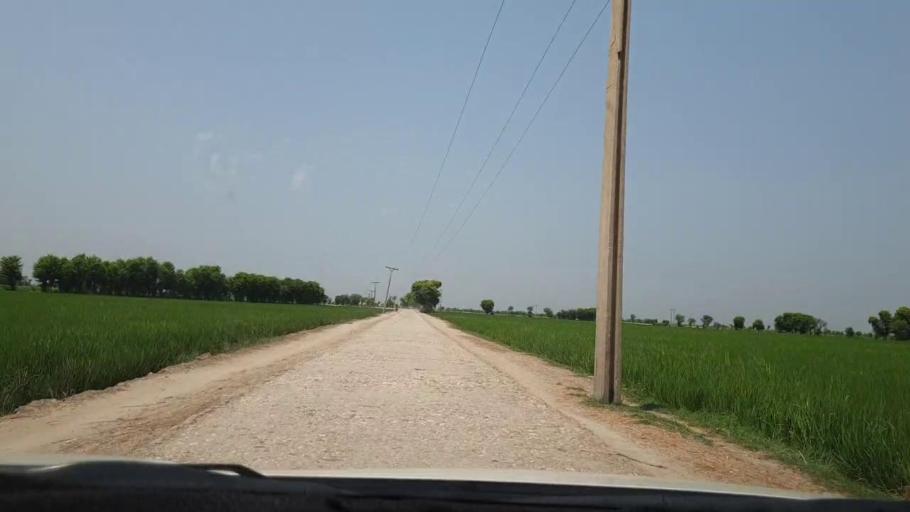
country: PK
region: Sindh
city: Radhan
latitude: 27.2482
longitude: 67.9845
